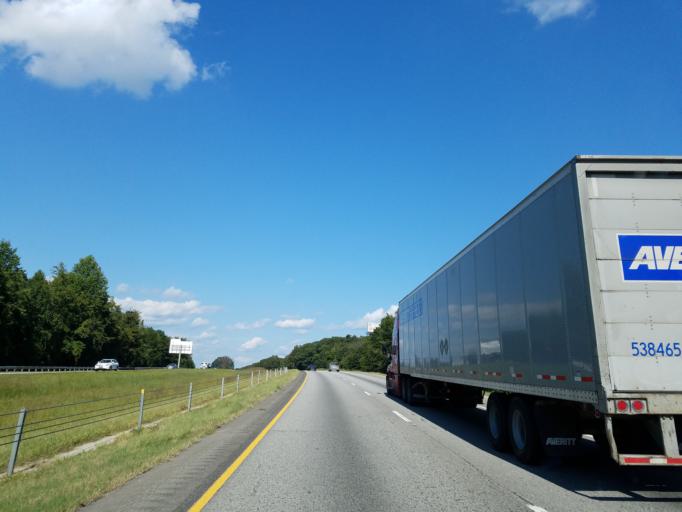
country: US
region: Georgia
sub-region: Franklin County
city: Carnesville
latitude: 34.3496
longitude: -83.3096
